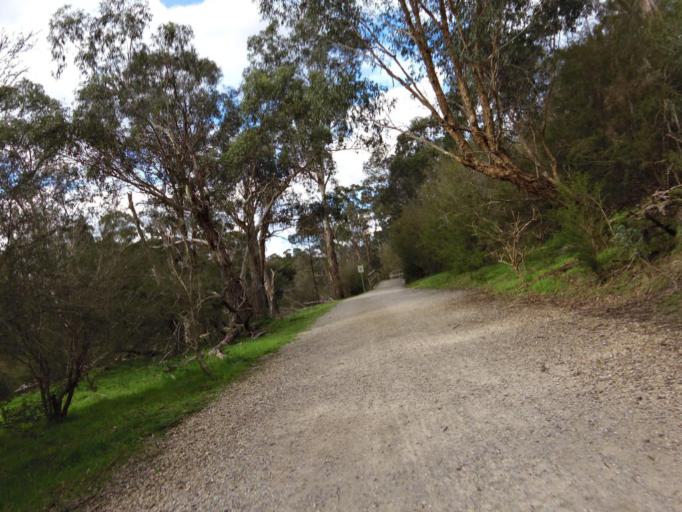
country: AU
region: Victoria
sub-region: Nillumbik
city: Eltham
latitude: -37.7392
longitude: 145.1437
